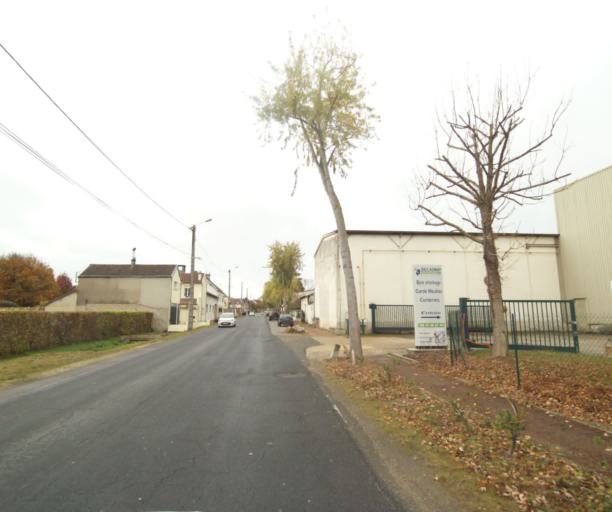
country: FR
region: Centre
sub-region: Departement d'Eure-et-Loir
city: Dreux
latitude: 48.7420
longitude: 1.3791
